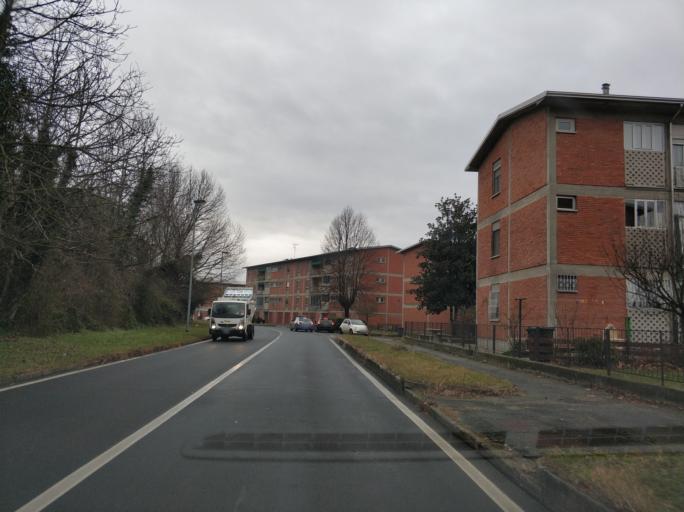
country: IT
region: Piedmont
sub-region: Provincia di Torino
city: Banchette
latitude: 45.4437
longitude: 7.8719
